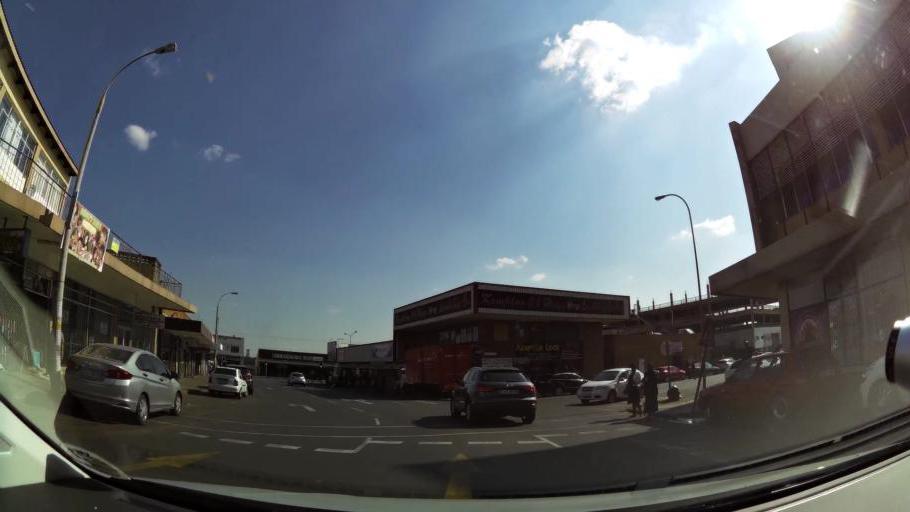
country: ZA
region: Gauteng
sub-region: City of Johannesburg Metropolitan Municipality
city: Modderfontein
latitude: -26.1044
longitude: 28.2279
